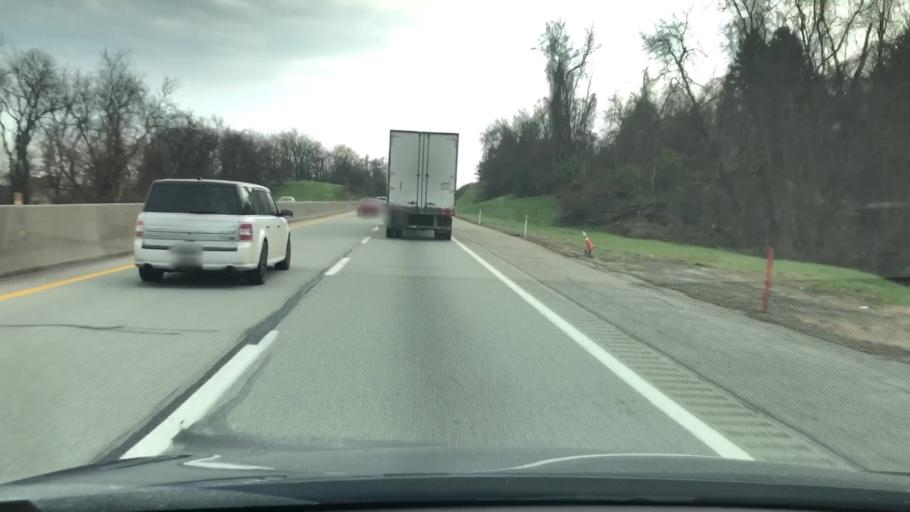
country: US
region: Pennsylvania
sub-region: Allegheny County
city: Plum
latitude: 40.4559
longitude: -79.7565
